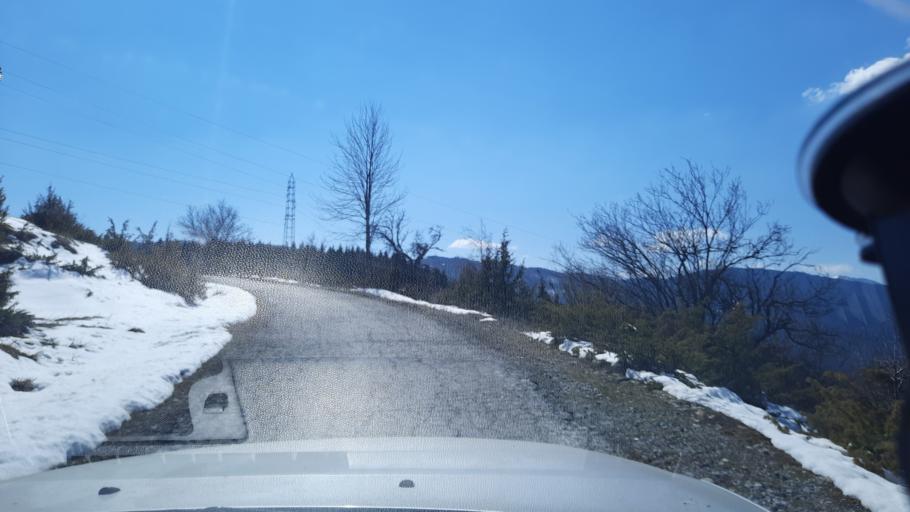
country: MK
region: Gostivar
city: Vrutok
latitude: 41.7158
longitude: 20.7258
